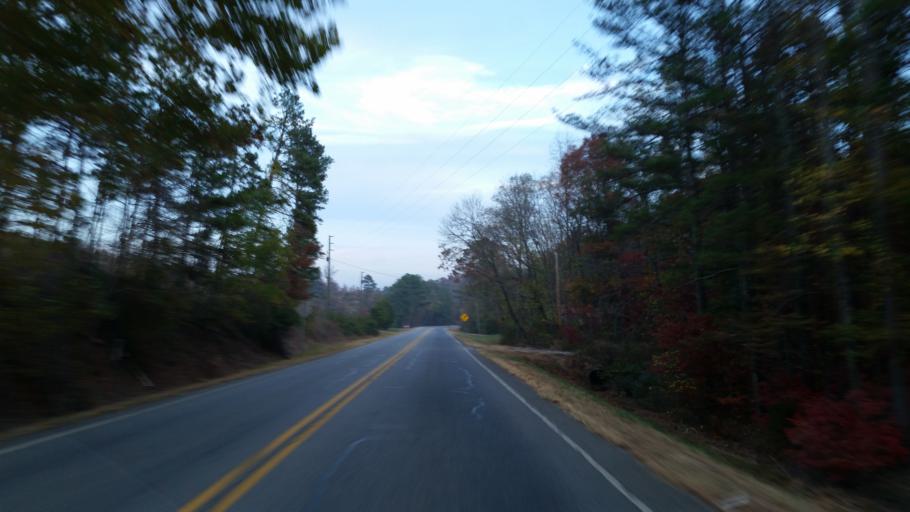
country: US
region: Georgia
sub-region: Murray County
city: Chatsworth
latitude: 34.5906
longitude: -84.7410
